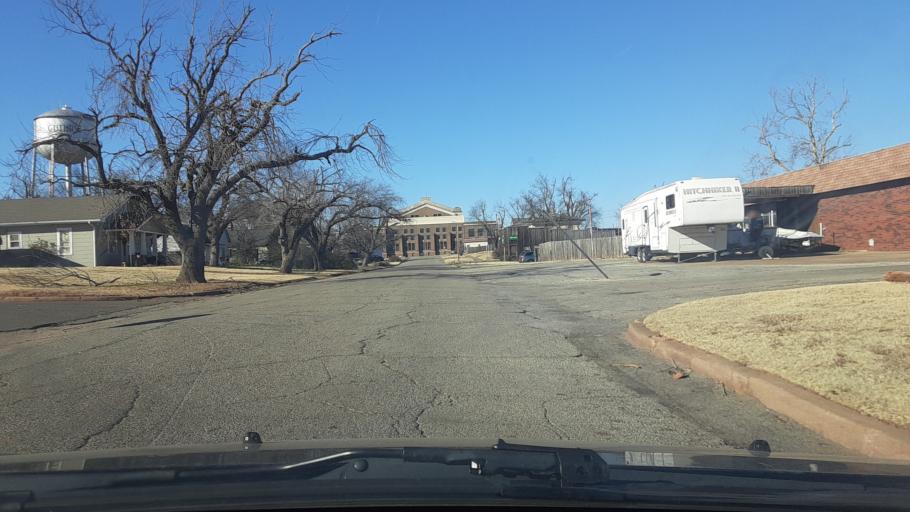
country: US
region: Oklahoma
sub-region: Logan County
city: Guthrie
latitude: 35.8781
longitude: -97.4096
